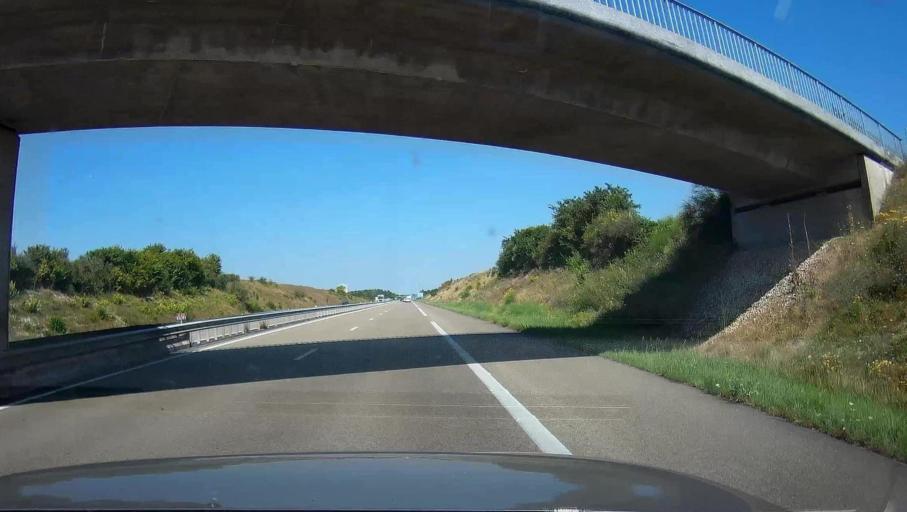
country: FR
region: Champagne-Ardenne
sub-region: Departement de l'Aube
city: Creney-pres-Troyes
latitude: 48.3975
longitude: 4.1514
